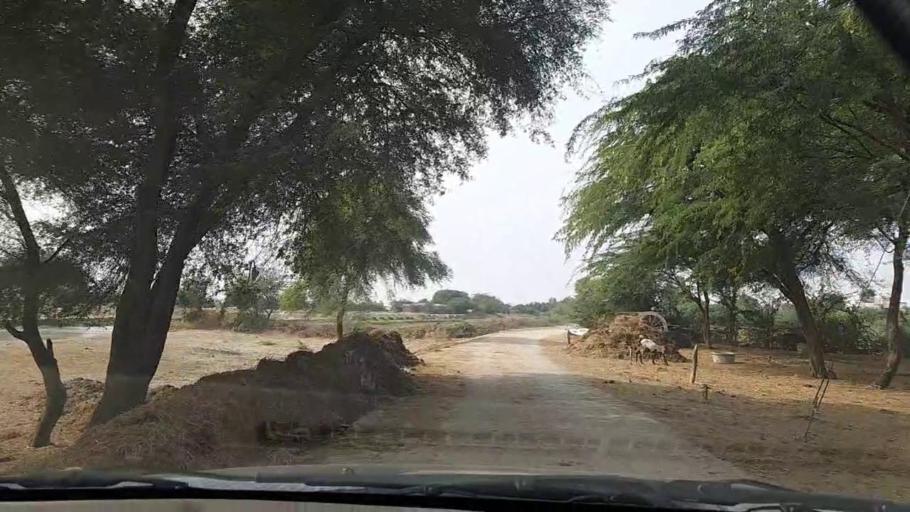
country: PK
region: Sindh
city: Thatta
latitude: 24.5684
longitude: 67.8619
